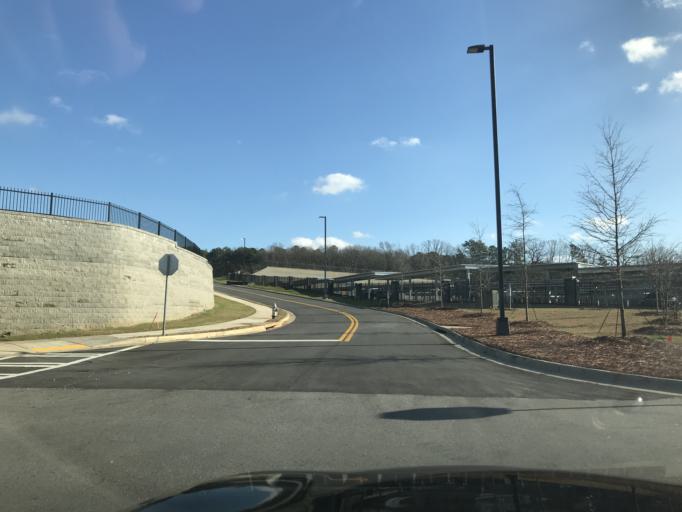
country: US
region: Georgia
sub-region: Fulton County
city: College Park
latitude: 33.6509
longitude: -84.4756
